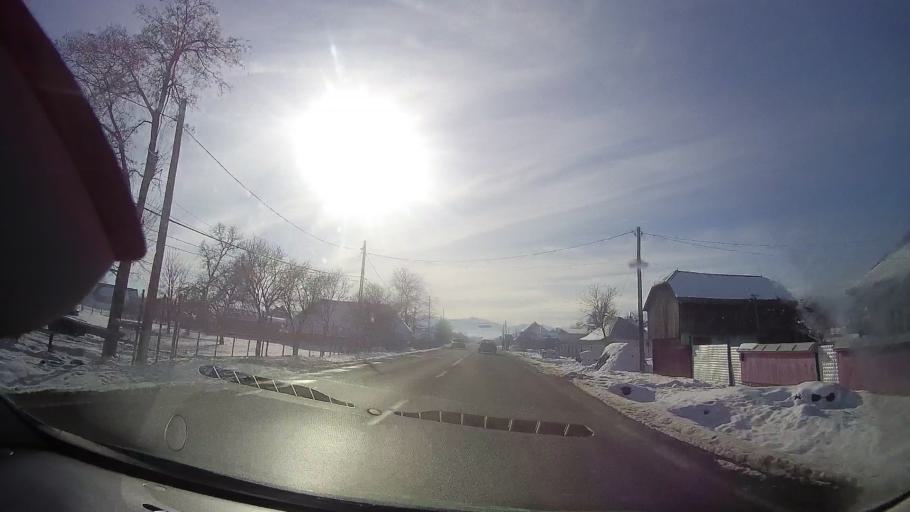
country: RO
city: Vanatori-Neamt
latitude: 47.1748
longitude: 26.3261
